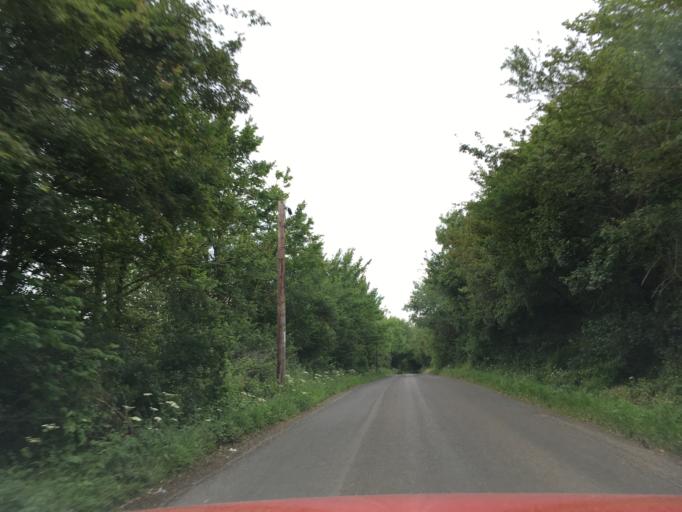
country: GB
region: England
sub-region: Wiltshire
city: Norton
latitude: 51.5893
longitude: -2.1774
